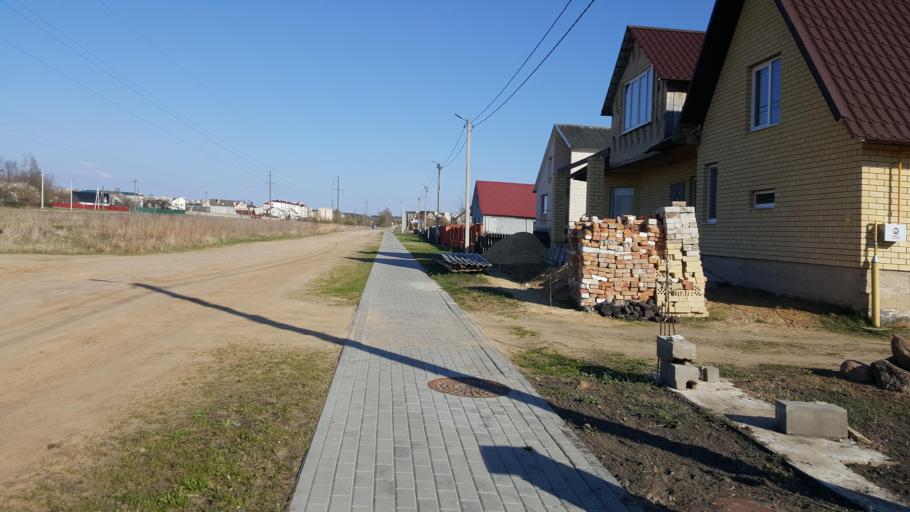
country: BY
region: Brest
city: Kamyanyets
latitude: 52.3948
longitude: 23.8093
